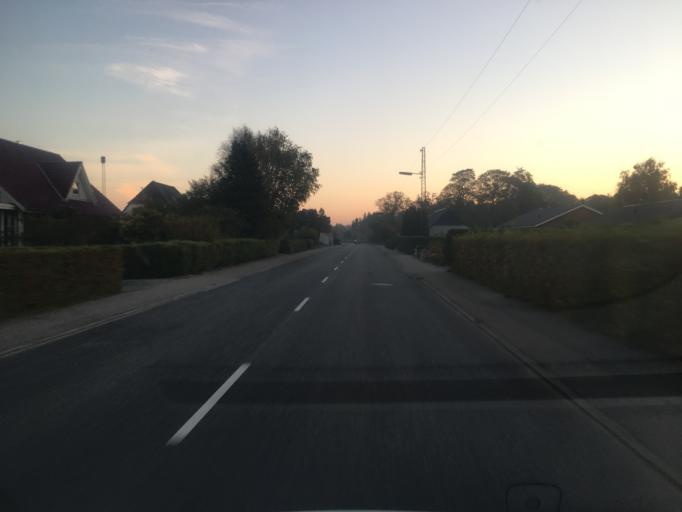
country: DE
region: Schleswig-Holstein
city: Bramstedtlund
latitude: 54.9504
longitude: 9.1015
